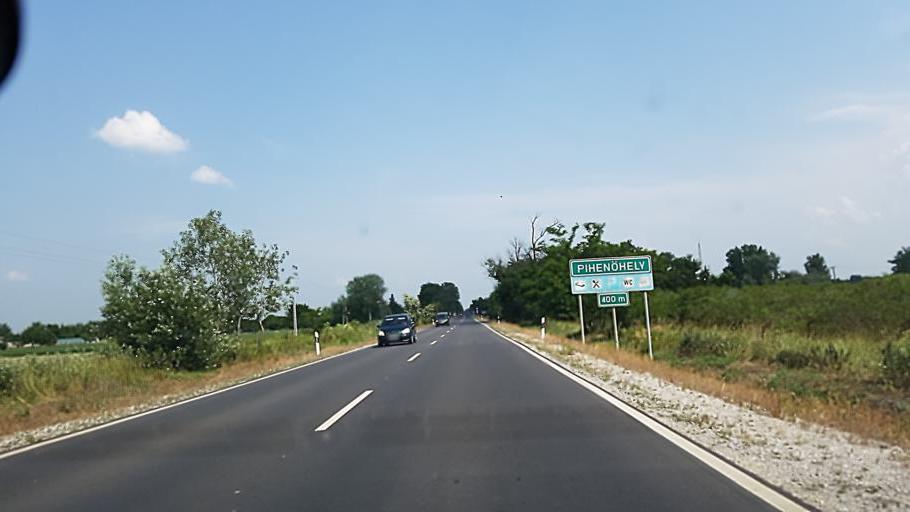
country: HU
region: Heves
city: Besenyotelek
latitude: 47.6802
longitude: 20.5038
